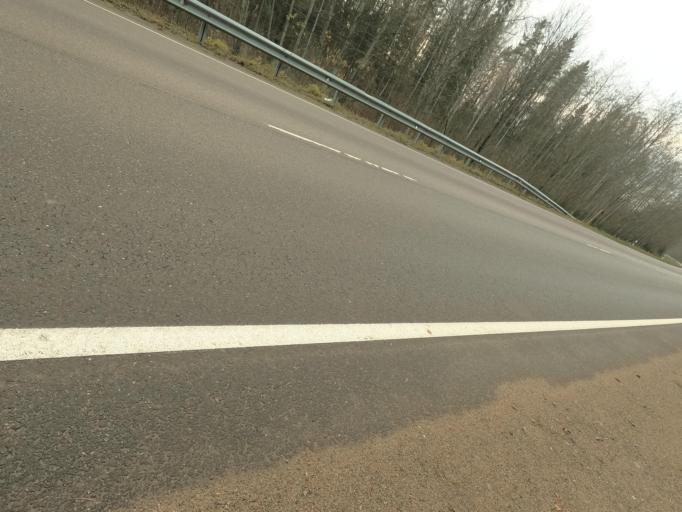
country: RU
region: Leningrad
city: Pavlovo
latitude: 59.8102
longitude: 30.9598
